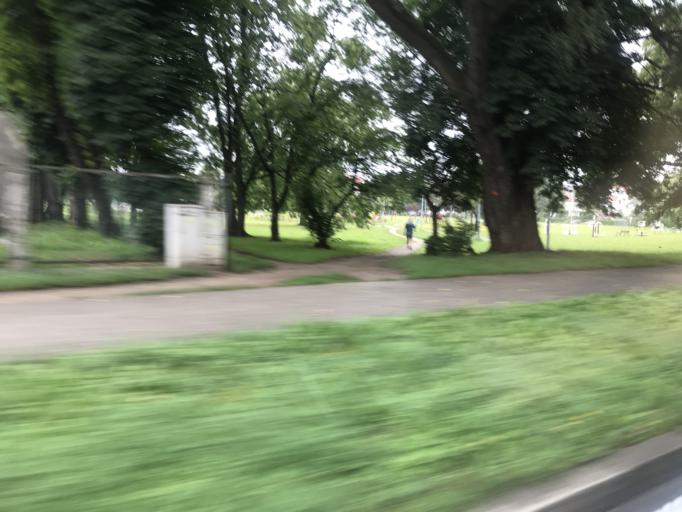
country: PL
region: Warmian-Masurian Voivodeship
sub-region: Powiat elblaski
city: Elblag
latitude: 54.1560
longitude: 19.4203
